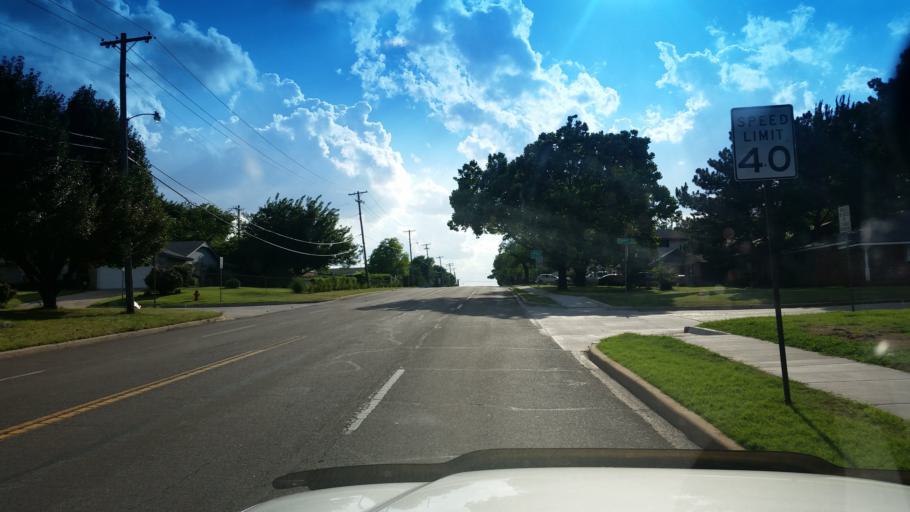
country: US
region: Oklahoma
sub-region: Oklahoma County
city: Nichols Hills
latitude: 35.5369
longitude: -97.5077
